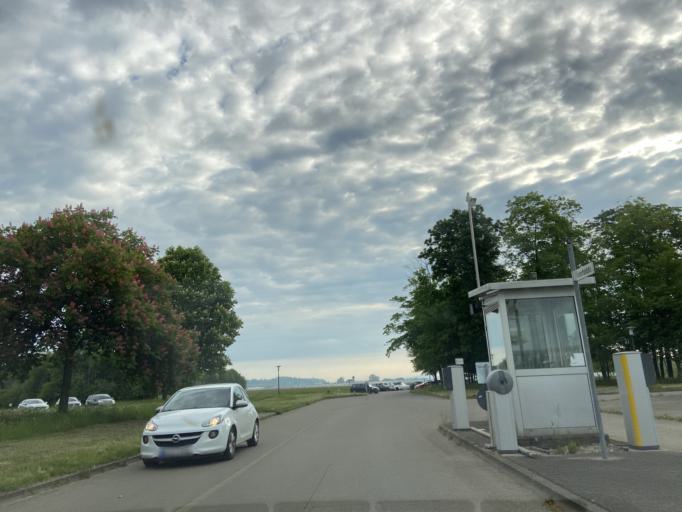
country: DE
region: Baden-Wuerttemberg
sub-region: Tuebingen Region
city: Hohentengen
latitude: 48.0455
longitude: 9.3669
